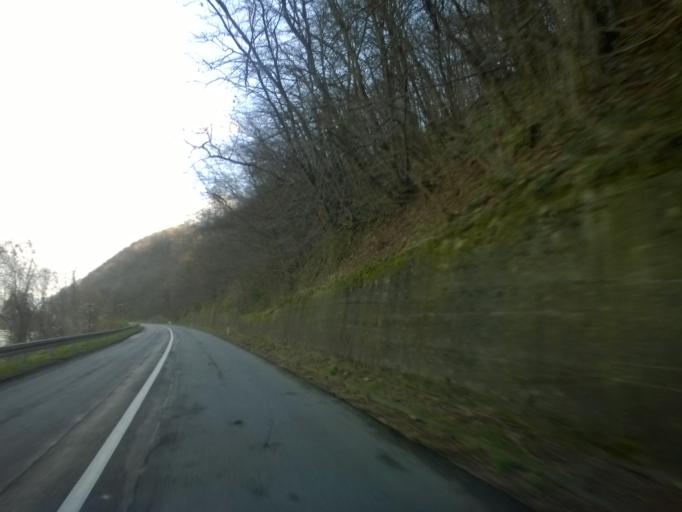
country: RS
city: Radenka
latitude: 44.6554
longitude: 21.7823
